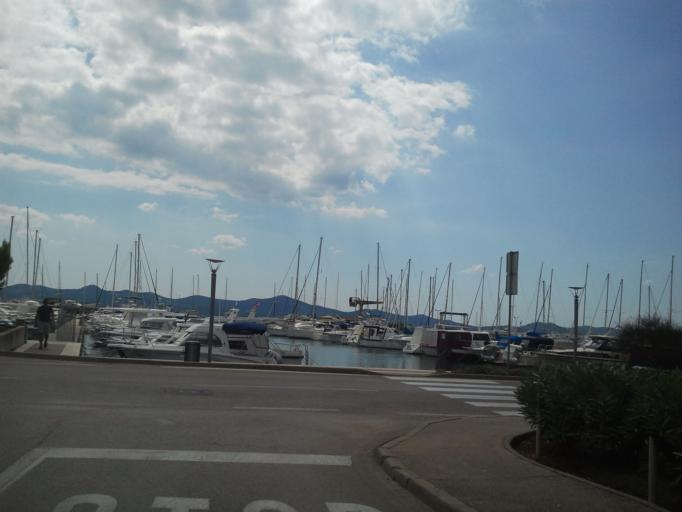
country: HR
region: Zadarska
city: Zadar
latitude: 44.1277
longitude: 15.2171
